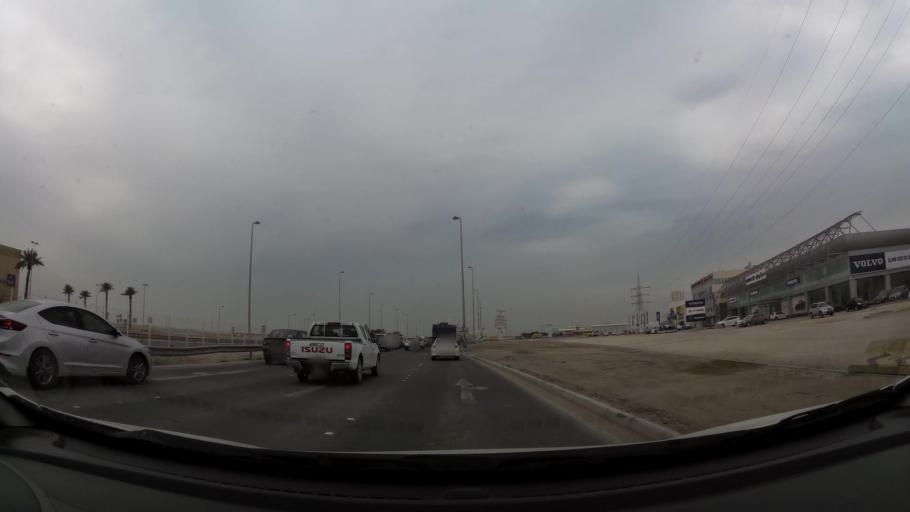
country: BH
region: Northern
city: Sitrah
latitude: 26.1706
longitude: 50.6028
